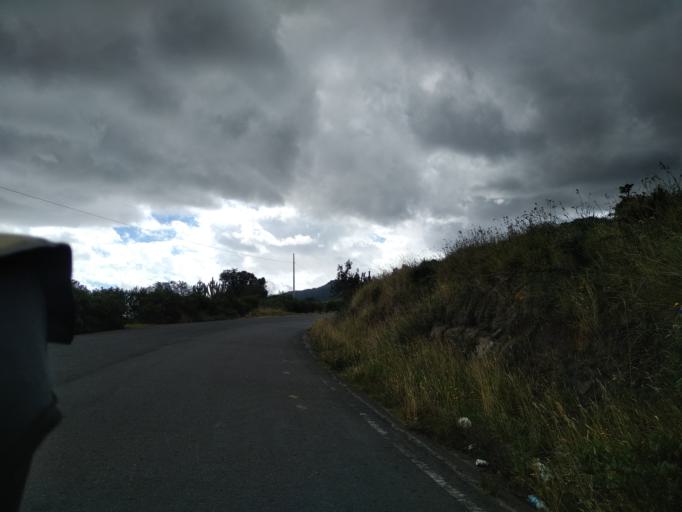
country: EC
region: Cotopaxi
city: Saquisili
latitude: -0.7189
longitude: -78.7629
